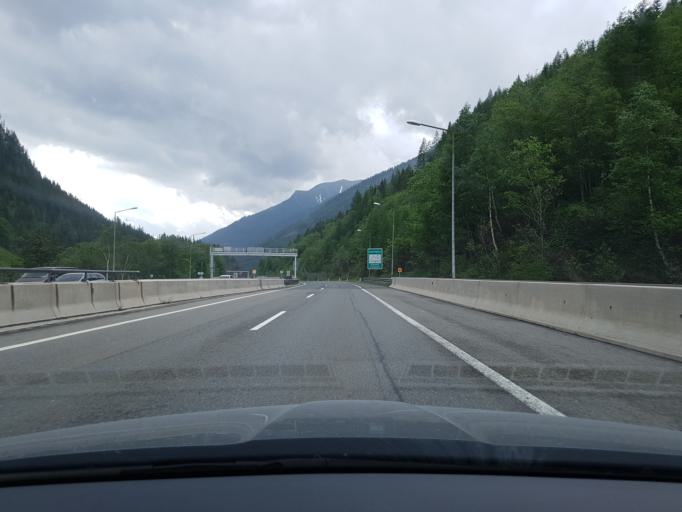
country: AT
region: Salzburg
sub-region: Politischer Bezirk Tamsweg
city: Zederhaus
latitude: 47.1806
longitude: 13.4401
